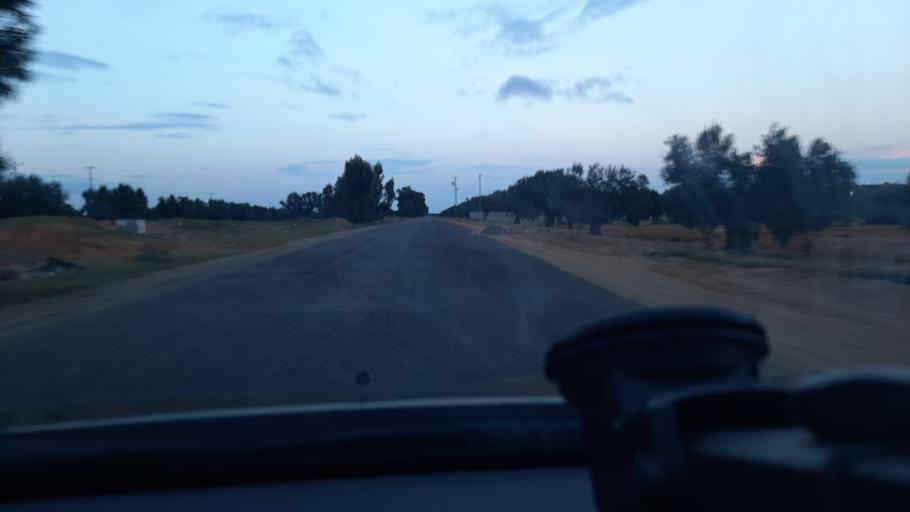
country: TN
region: Al Mahdiyah
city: Shurban
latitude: 34.9742
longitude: 10.3764
